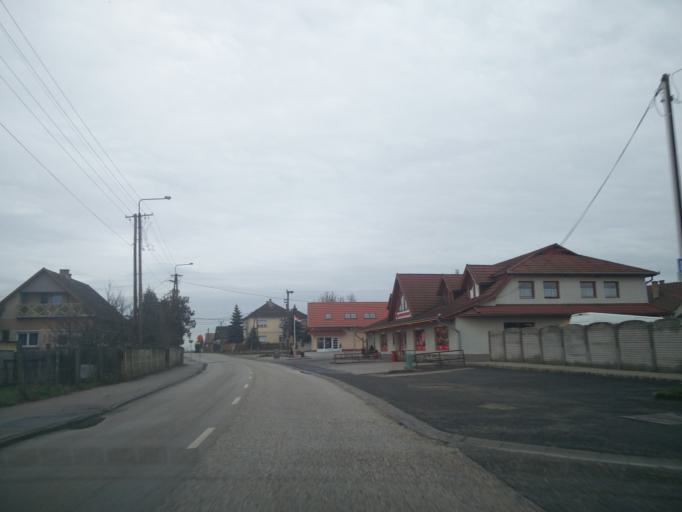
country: HU
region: Pest
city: Koka
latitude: 47.4859
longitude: 19.5784
